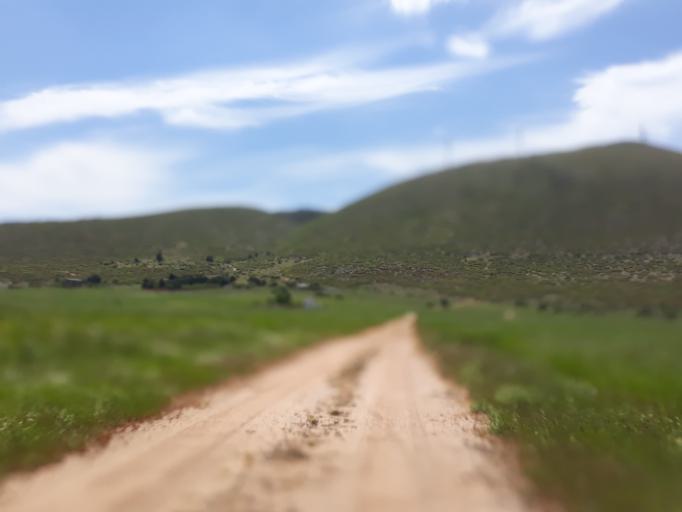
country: GR
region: Central Greece
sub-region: Nomos Voiotias
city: Ayios Thomas
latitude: 38.1853
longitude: 23.5615
